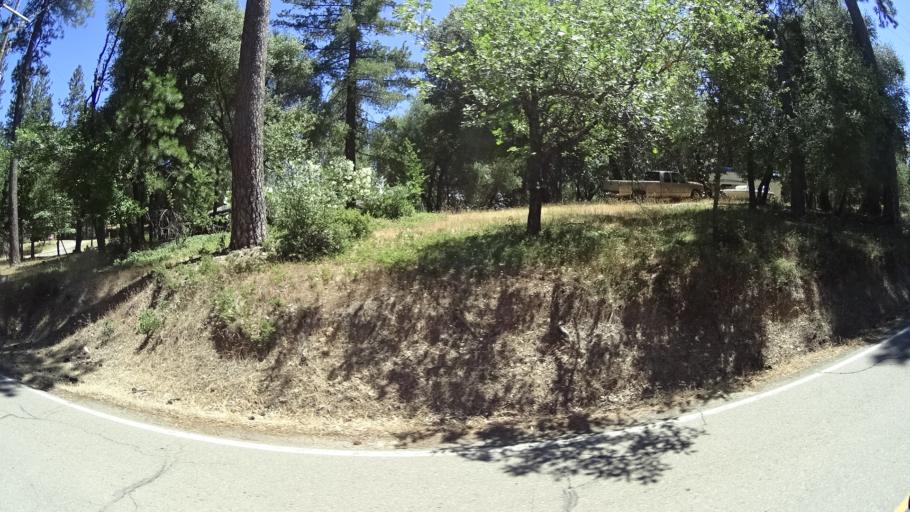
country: US
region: California
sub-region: Amador County
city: Pioneer
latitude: 38.3751
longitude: -120.5098
